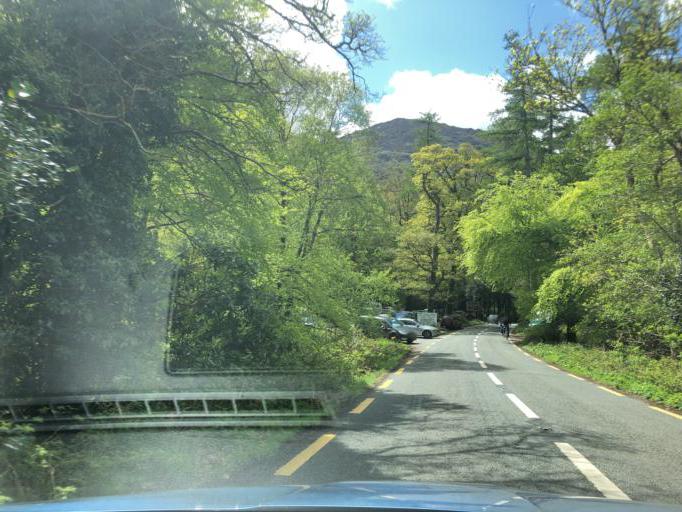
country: IE
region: Munster
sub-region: Ciarrai
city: Cill Airne
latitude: 52.0066
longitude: -9.5050
